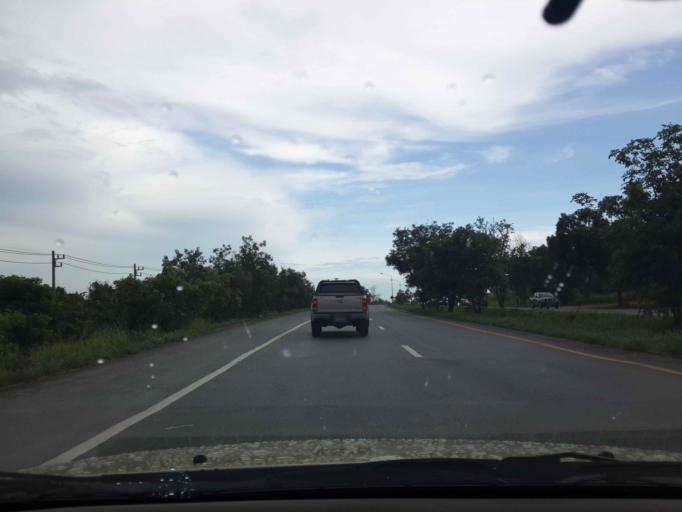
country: TH
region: Chon Buri
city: Phatthaya
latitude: 12.9262
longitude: 101.0053
